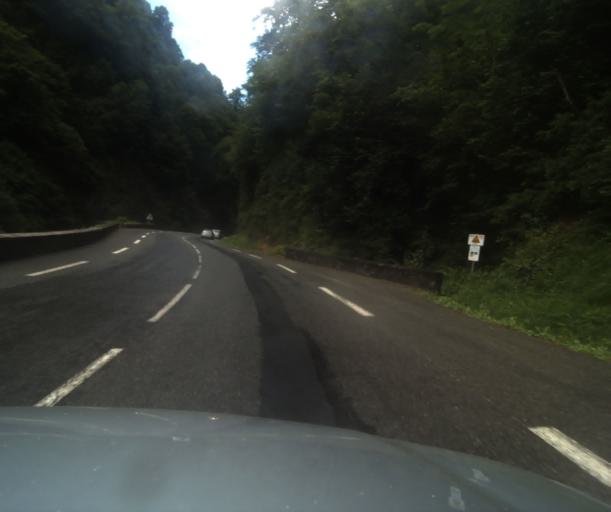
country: FR
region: Midi-Pyrenees
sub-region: Departement des Hautes-Pyrenees
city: Pierrefitte-Nestalas
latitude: 42.9368
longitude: -0.0487
